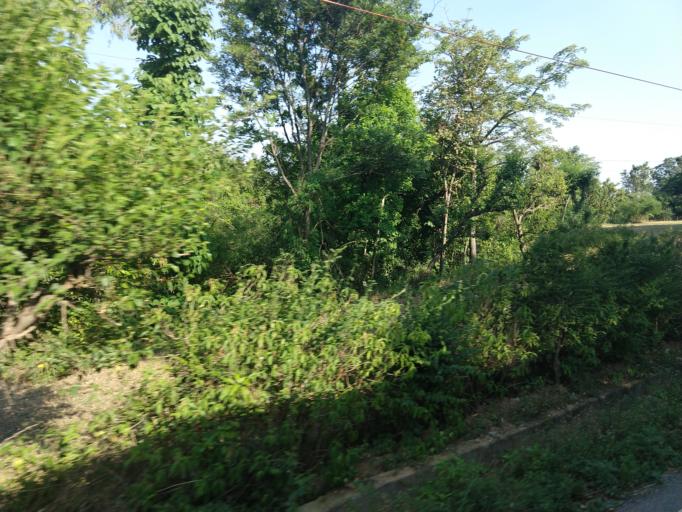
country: IN
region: Himachal Pradesh
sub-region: Chamba
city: Chowari
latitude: 32.3582
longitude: 75.9204
